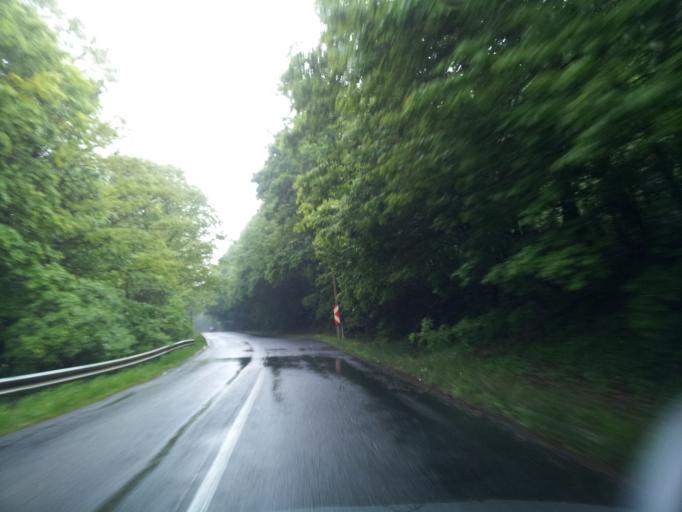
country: HU
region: Baranya
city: Hosszuheteny
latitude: 46.1750
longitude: 18.3243
